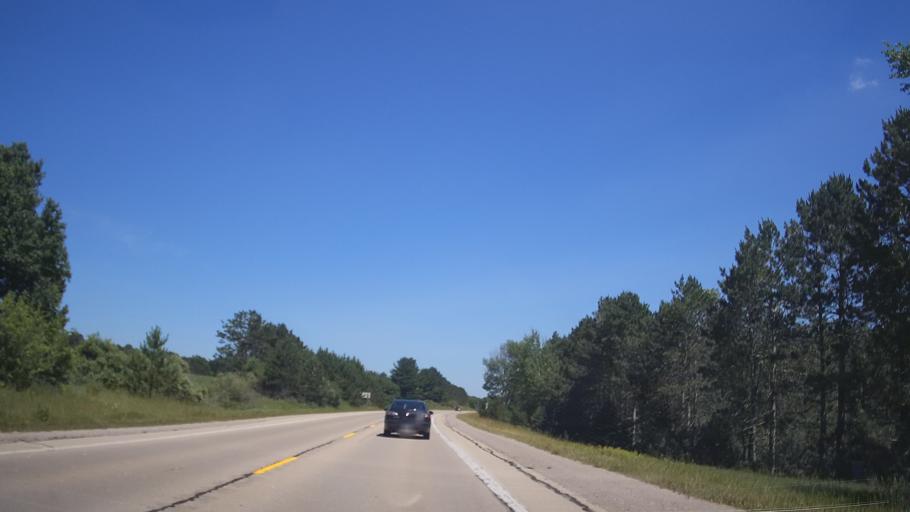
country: US
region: Michigan
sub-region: Clare County
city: Clare
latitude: 43.8699
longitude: -84.9257
